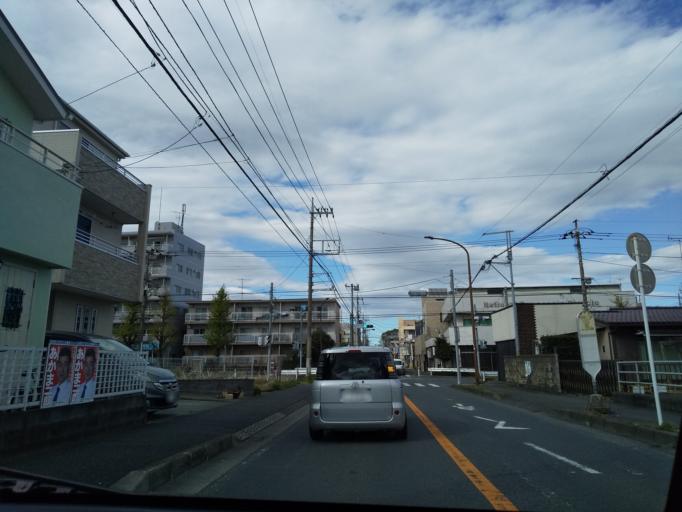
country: JP
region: Kanagawa
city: Zama
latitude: 35.5663
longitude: 139.3756
